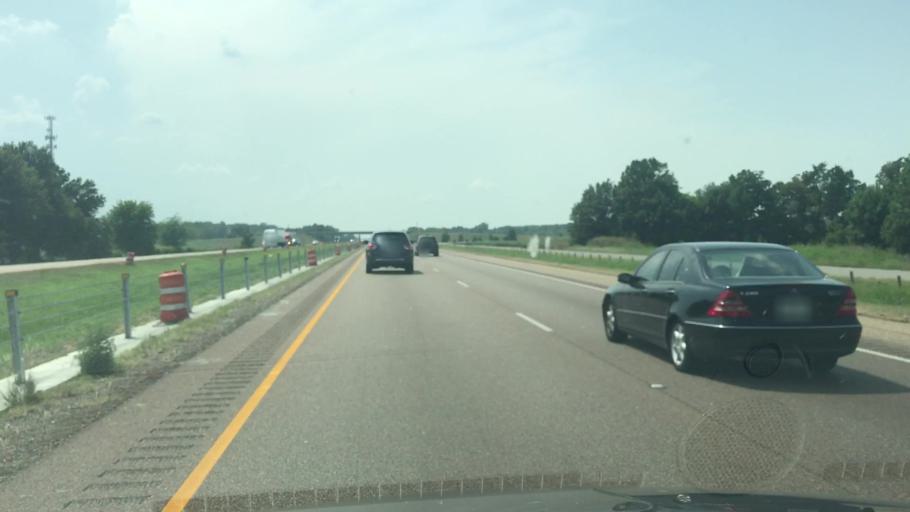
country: US
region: Arkansas
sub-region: Crittenden County
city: Earle
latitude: 35.1497
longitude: -90.3576
